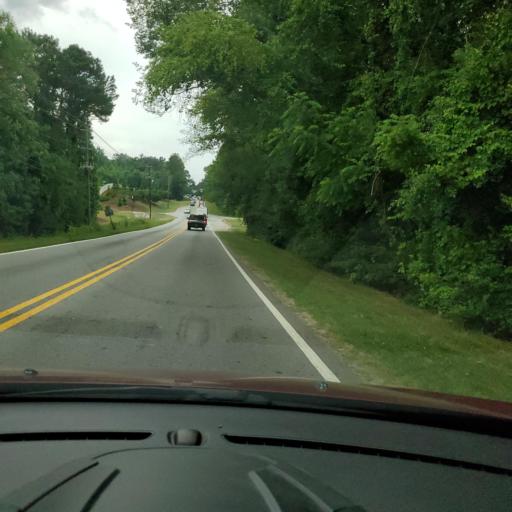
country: US
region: Georgia
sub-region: Henry County
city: Stockbridge
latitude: 33.5289
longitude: -84.2268
